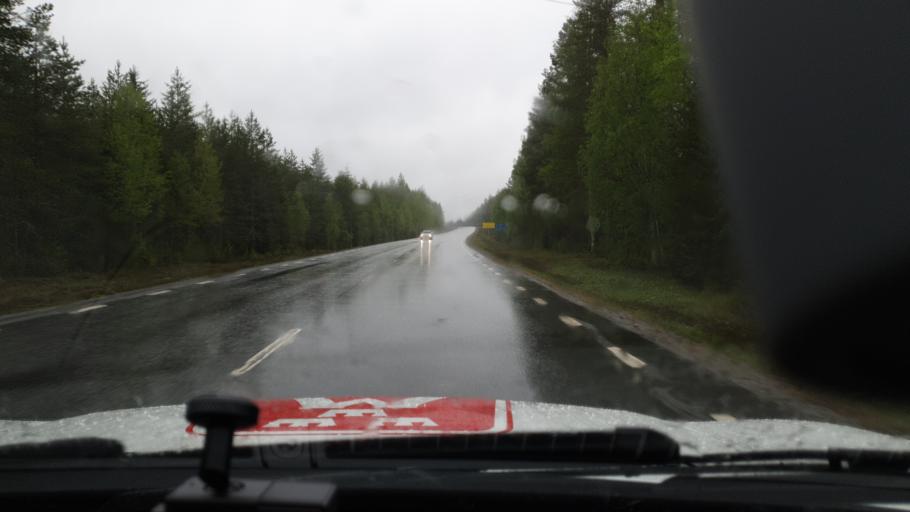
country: SE
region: Vaesterbotten
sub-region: Vannas Kommun
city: Vannasby
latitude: 64.0699
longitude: 19.9916
